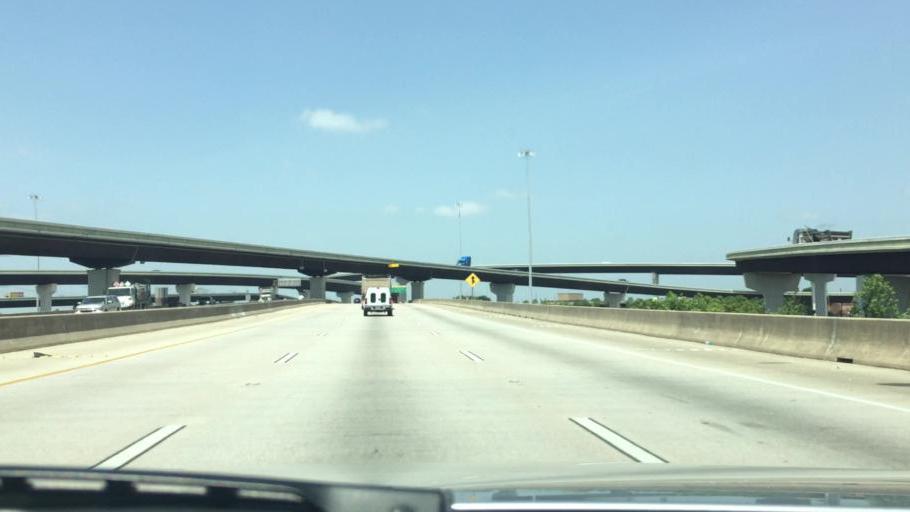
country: US
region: Texas
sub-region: Harris County
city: Aldine
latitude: 29.9408
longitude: -95.4112
